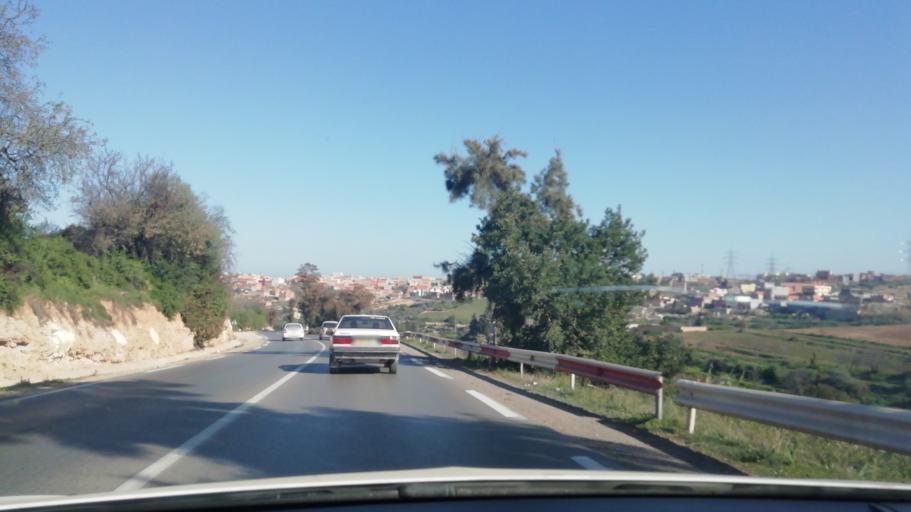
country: DZ
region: Tlemcen
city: Nedroma
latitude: 35.0811
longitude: -1.8729
